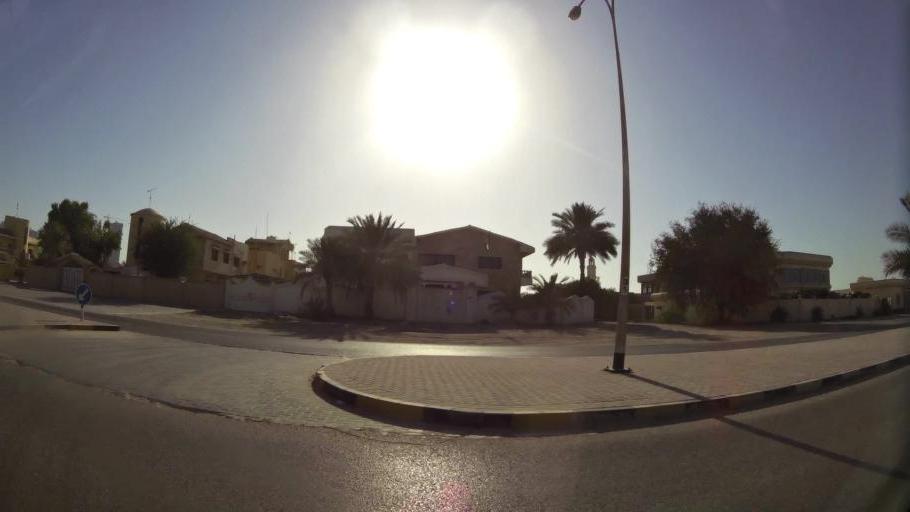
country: AE
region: Ajman
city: Ajman
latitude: 25.4016
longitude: 55.4628
